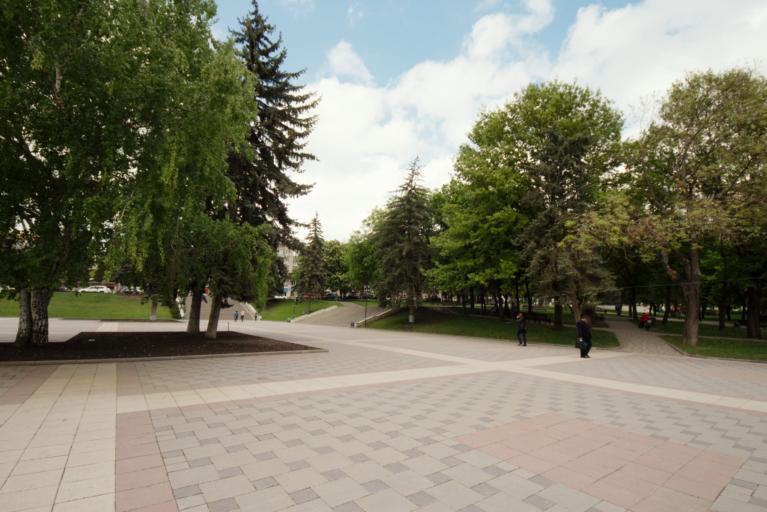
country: RU
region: Stavropol'skiy
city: Pyatigorsk
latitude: 44.0395
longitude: 43.0709
